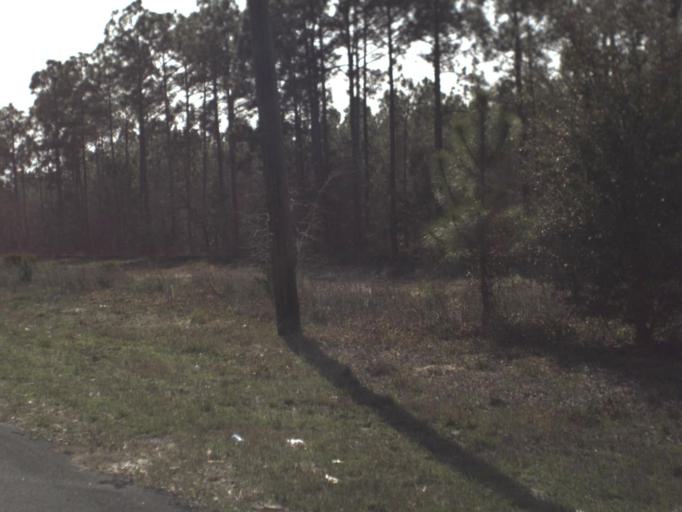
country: US
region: Florida
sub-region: Franklin County
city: Carrabelle
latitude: 29.9404
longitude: -84.5011
